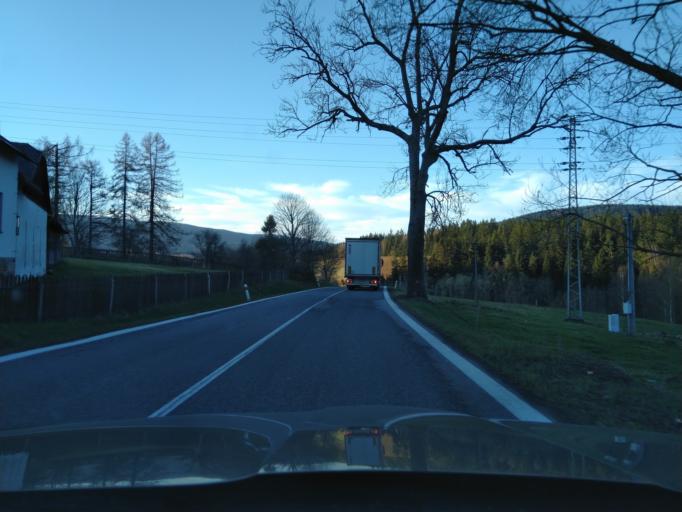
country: CZ
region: Jihocesky
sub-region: Okres Prachatice
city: Vimperk
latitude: 49.0283
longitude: 13.7649
